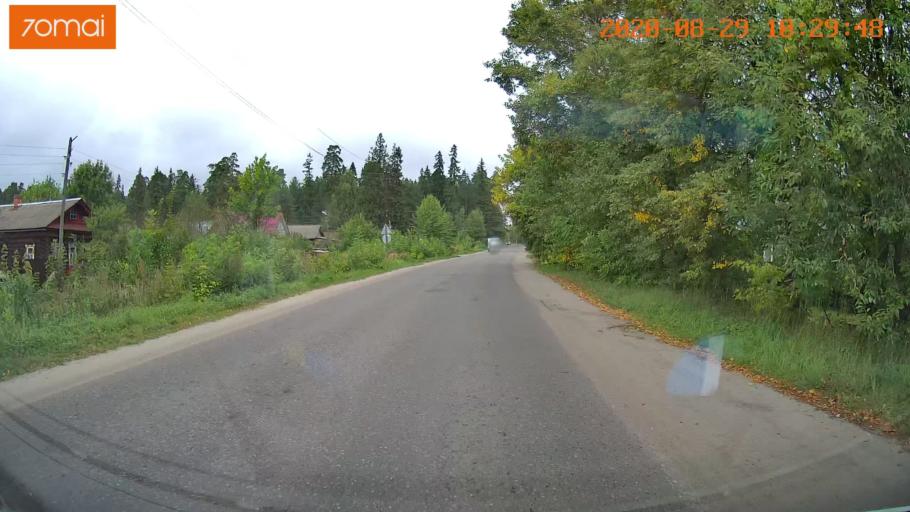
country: RU
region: Ivanovo
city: Yur'yevets
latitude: 57.3126
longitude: 43.0964
